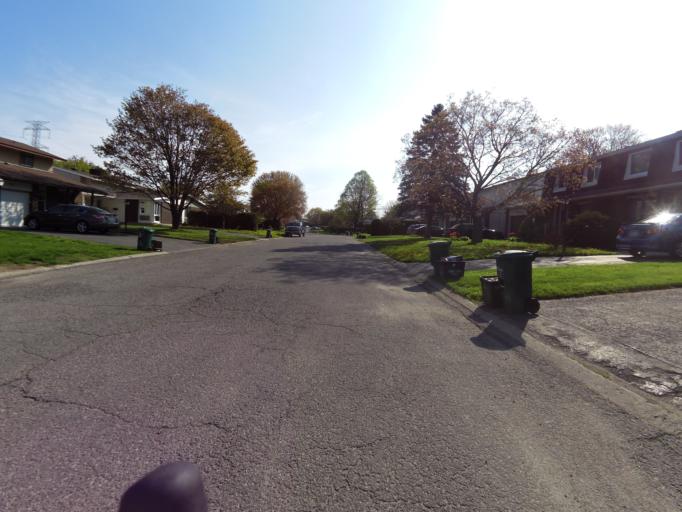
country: CA
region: Ontario
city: Ottawa
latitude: 45.3340
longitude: -75.7360
